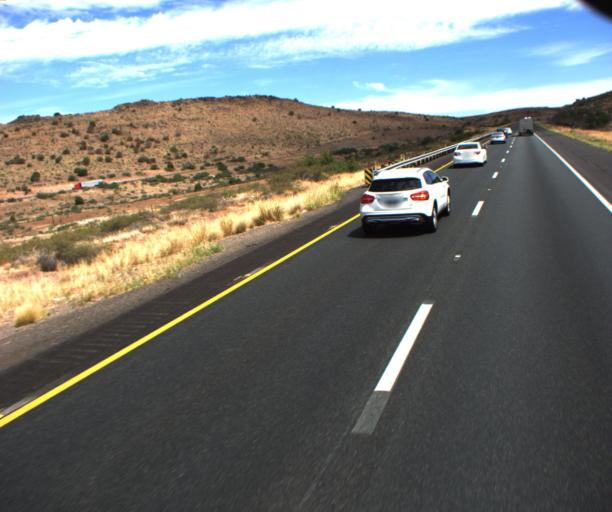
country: US
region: Arizona
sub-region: Yavapai County
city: Cordes Lakes
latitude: 34.4549
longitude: -112.0304
